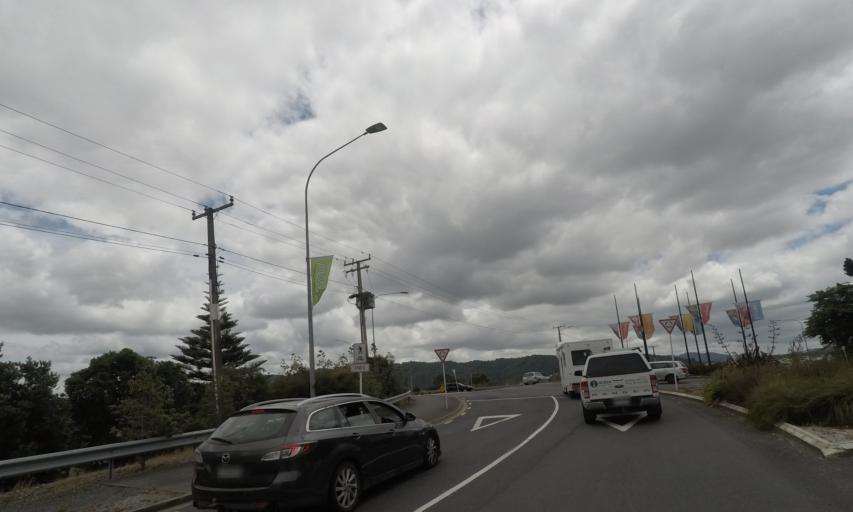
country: NZ
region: Northland
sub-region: Whangarei
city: Whangarei
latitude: -35.7338
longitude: 174.3276
